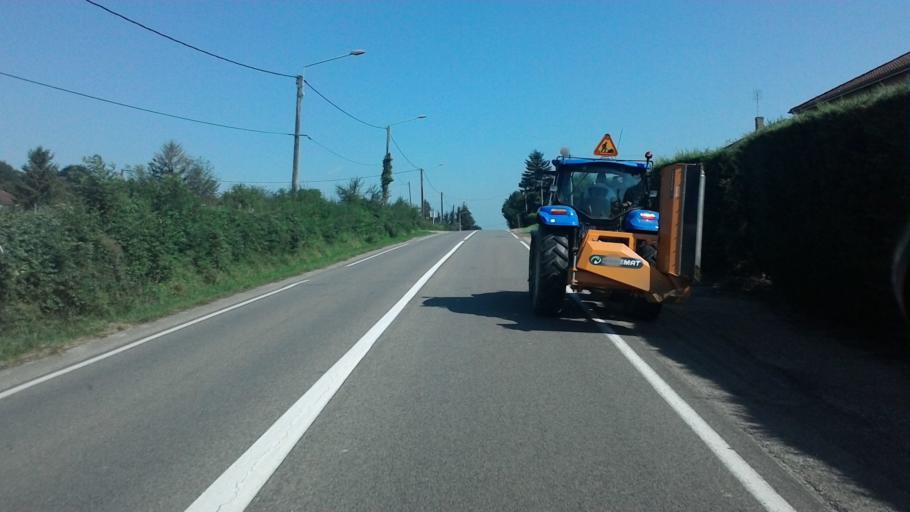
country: FR
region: Rhone-Alpes
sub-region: Departement de l'Ain
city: Montrevel-en-Bresse
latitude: 46.3700
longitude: 5.1205
